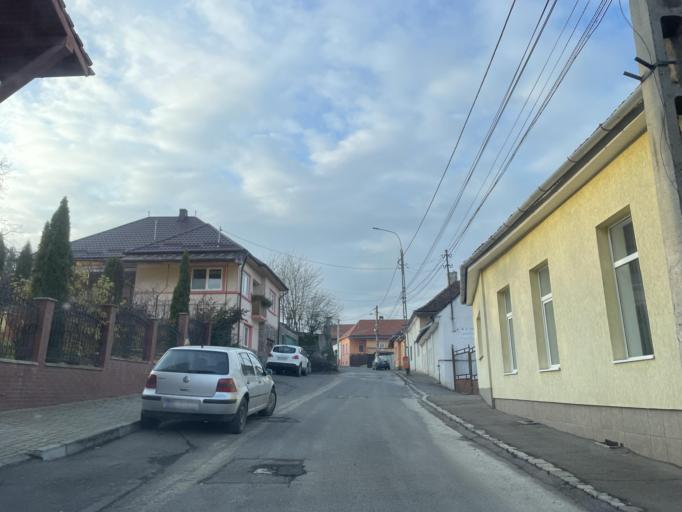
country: RO
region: Mures
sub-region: Municipiul Reghin
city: Reghin
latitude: 46.7841
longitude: 24.7018
